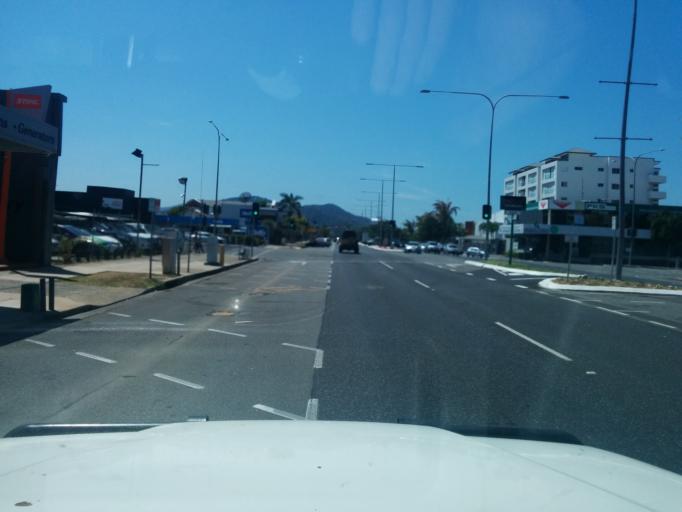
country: AU
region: Queensland
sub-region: Cairns
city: Cairns
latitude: -16.9225
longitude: 145.7726
